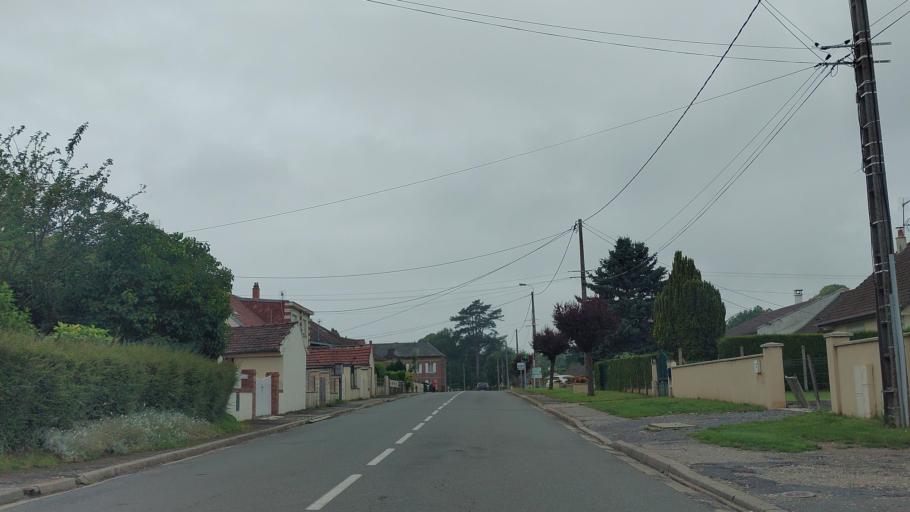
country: FR
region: Picardie
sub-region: Departement de la Somme
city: Bethencourt-sur-Mer
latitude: 50.0873
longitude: 1.4865
